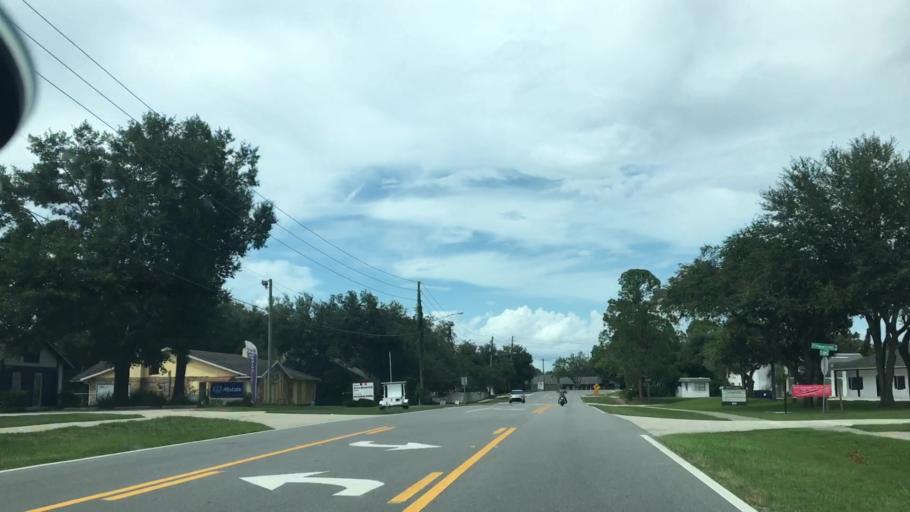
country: US
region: Florida
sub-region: Volusia County
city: Deltona
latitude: 28.8810
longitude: -81.2802
